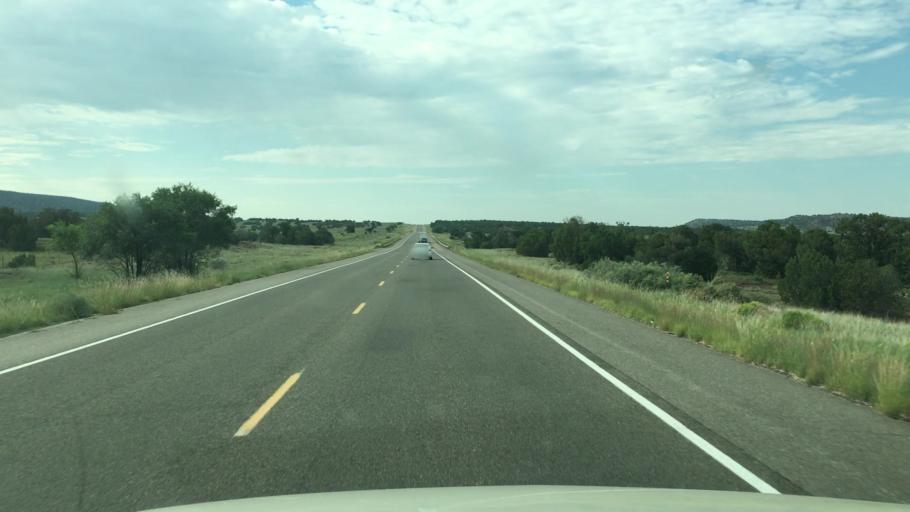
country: US
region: New Mexico
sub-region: Santa Fe County
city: Eldorado at Santa Fe
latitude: 35.3250
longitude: -105.8329
